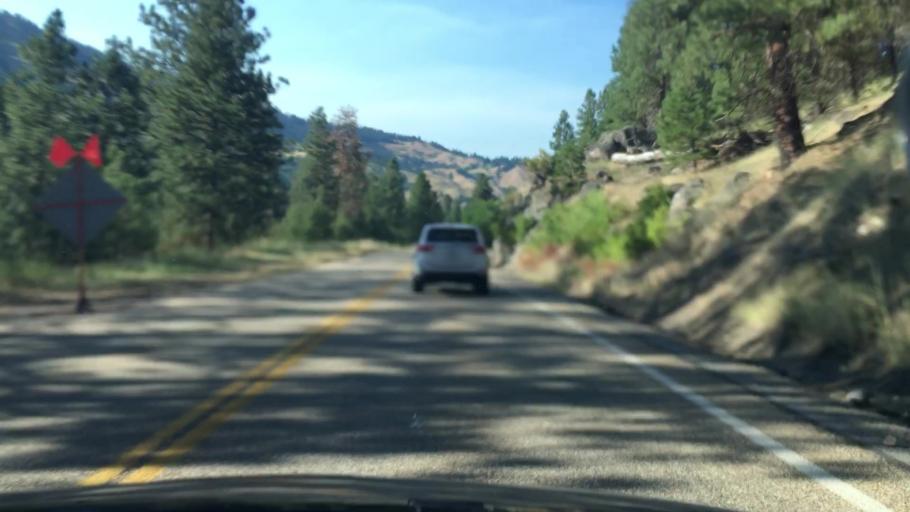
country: US
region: Idaho
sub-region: Boise County
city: Idaho City
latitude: 44.0659
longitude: -116.1206
